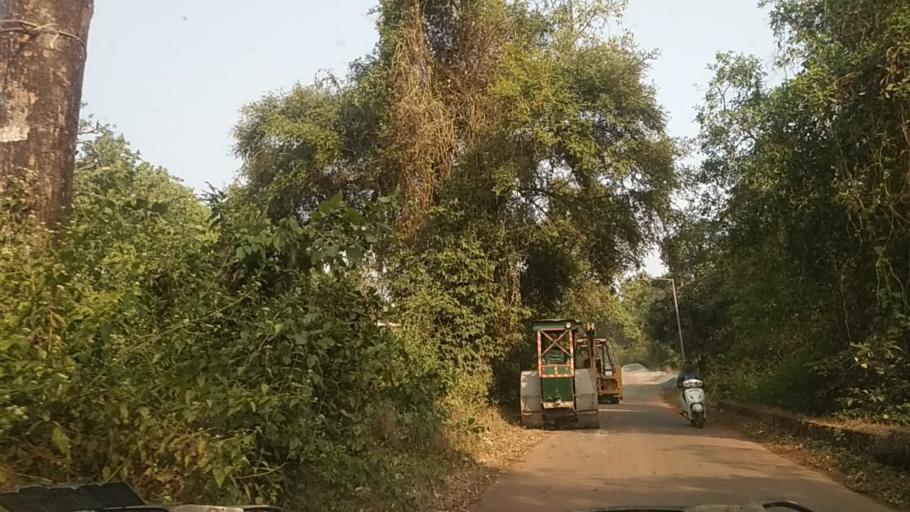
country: IN
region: Goa
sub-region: South Goa
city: Raia
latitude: 15.3165
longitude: 73.9473
